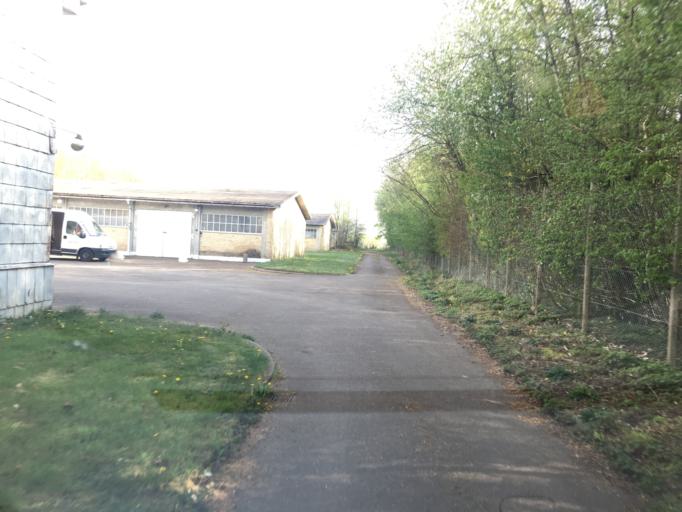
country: DK
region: South Denmark
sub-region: Tonder Kommune
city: Tonder
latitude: 54.9593
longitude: 8.8669
